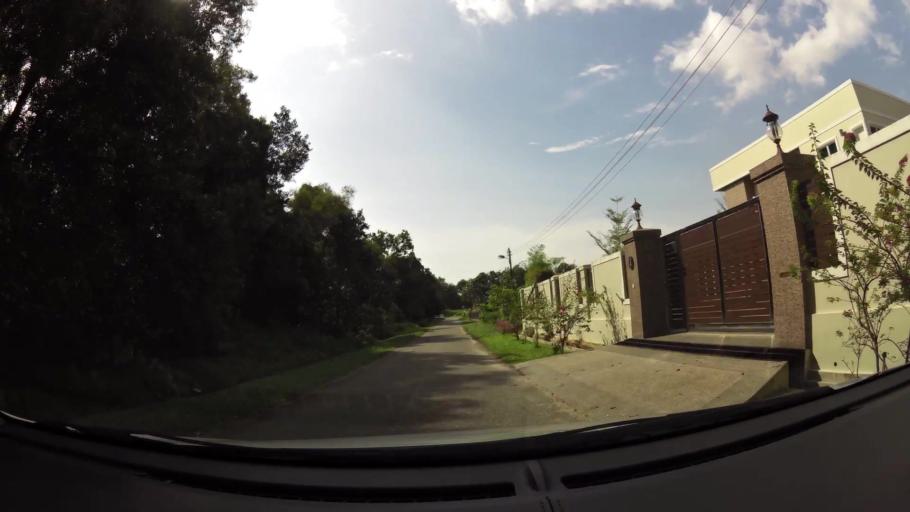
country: BN
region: Brunei and Muara
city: Bandar Seri Begawan
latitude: 4.9526
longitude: 114.9680
